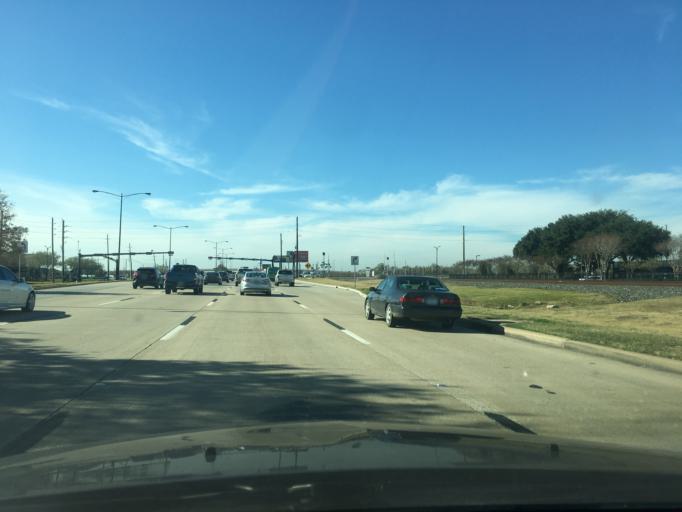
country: US
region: Texas
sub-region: Fort Bend County
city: Sugar Land
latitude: 29.6171
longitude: -95.6424
